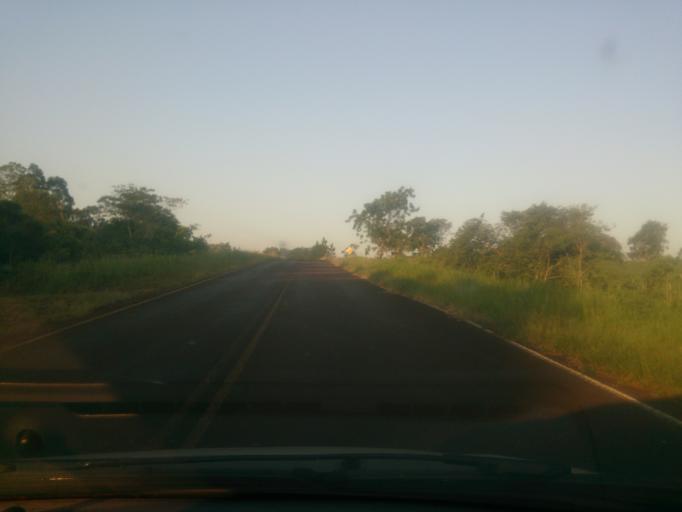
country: AR
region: Misiones
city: Panambi
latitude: -27.6640
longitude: -54.9121
